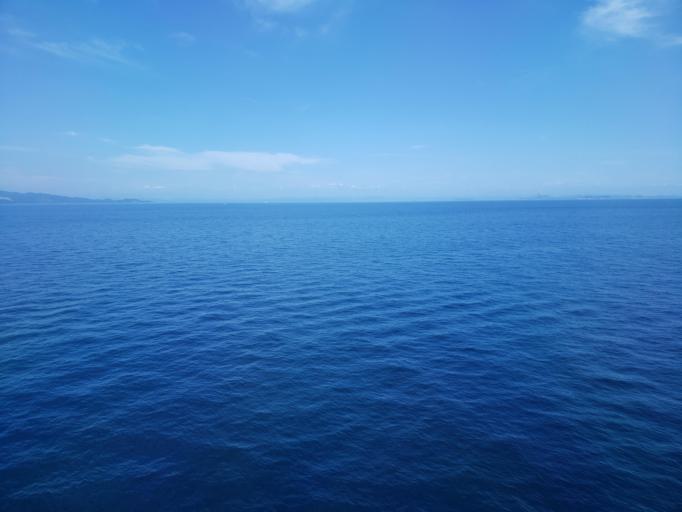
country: JP
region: Kagawa
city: Tonosho
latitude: 34.4607
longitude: 134.4657
